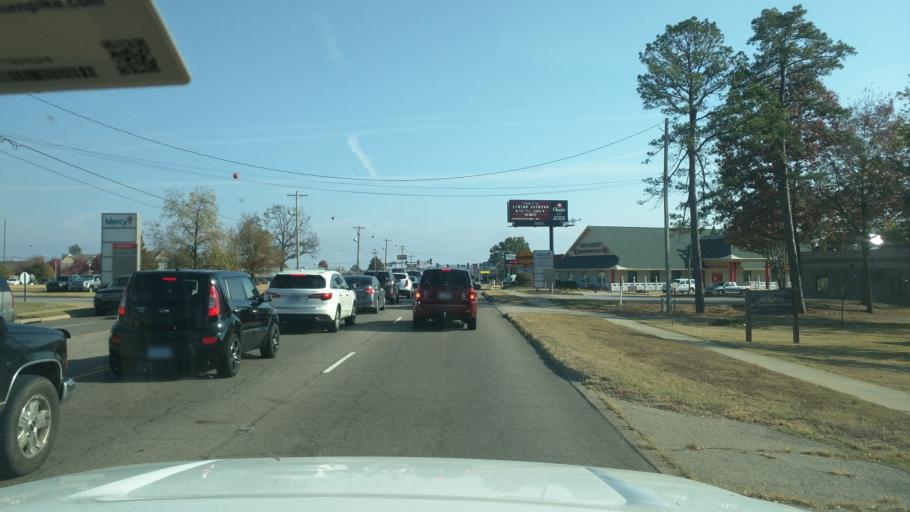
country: US
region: Arkansas
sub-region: Sebastian County
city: Fort Smith
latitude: 35.3538
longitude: -94.3534
